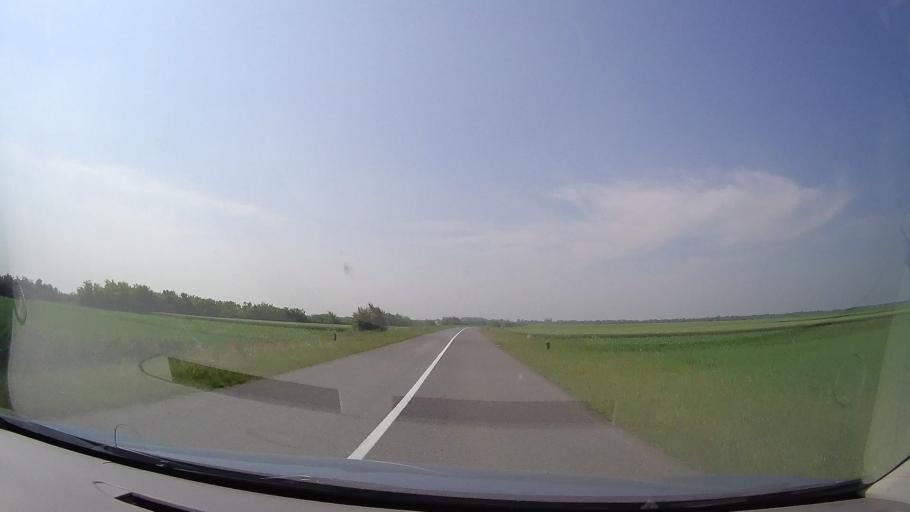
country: RS
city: Jarkovac
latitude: 45.2900
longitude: 20.7645
